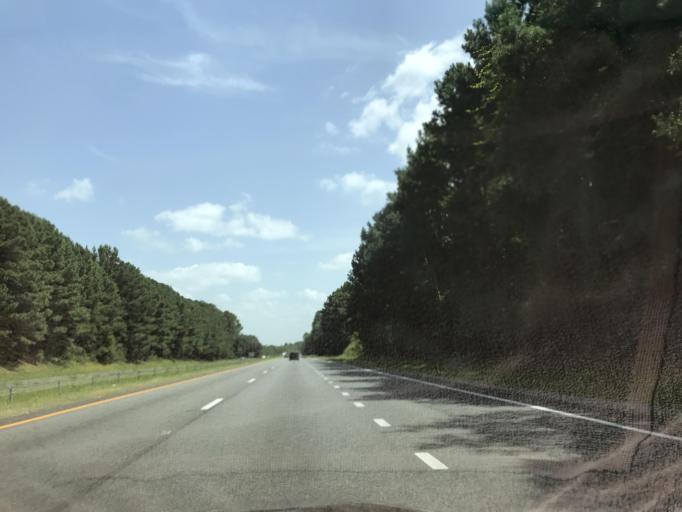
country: US
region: North Carolina
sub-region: Sampson County
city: Plain View
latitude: 35.2256
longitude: -78.3477
